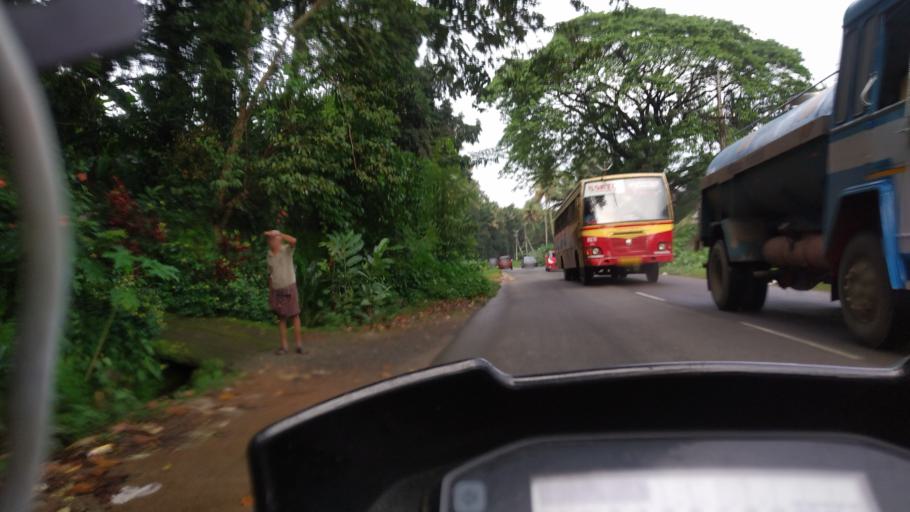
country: IN
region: Kerala
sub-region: Ernakulam
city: Kotamangalam
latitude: 10.0605
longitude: 76.6858
